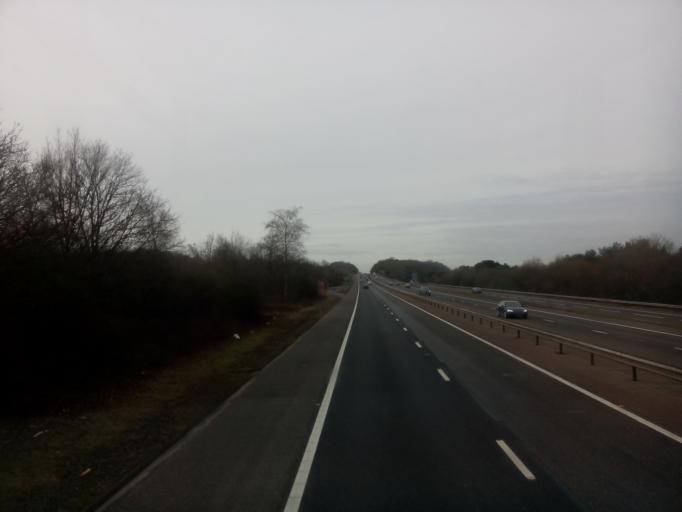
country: GB
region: England
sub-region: Hampshire
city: Overton
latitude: 51.2079
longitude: -1.1804
